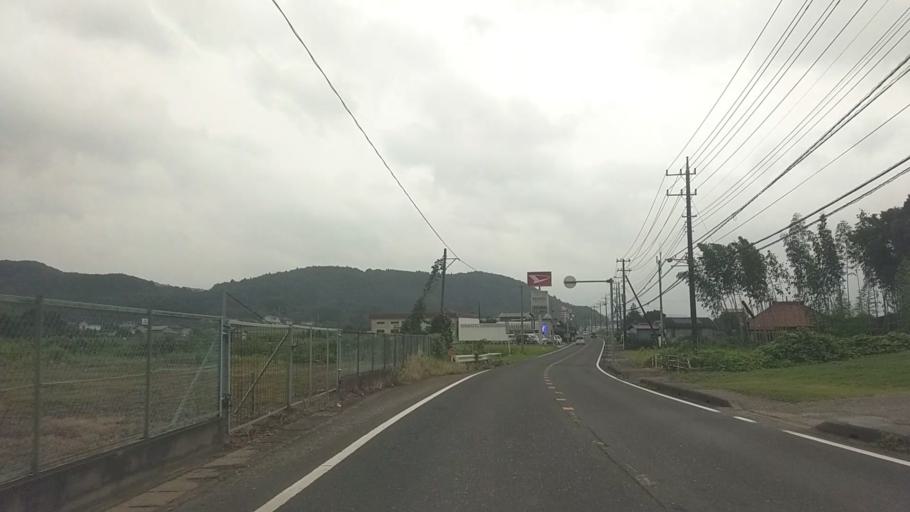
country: JP
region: Chiba
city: Kisarazu
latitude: 35.3106
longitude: 140.0646
